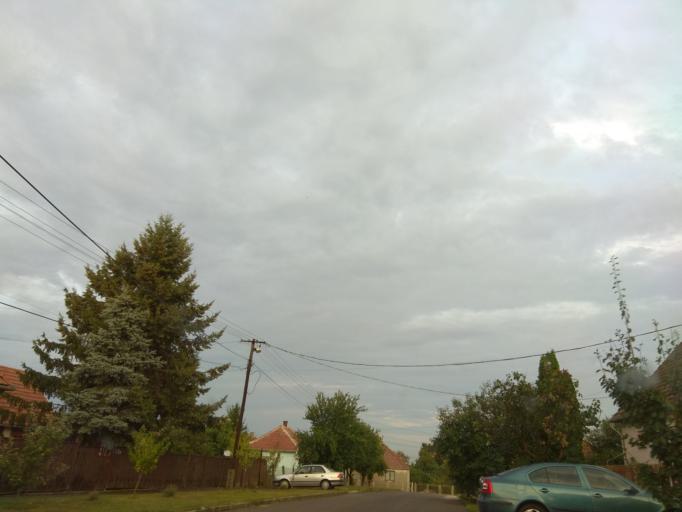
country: HU
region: Borsod-Abauj-Zemplen
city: Miskolc
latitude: 48.0512
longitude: 20.7924
